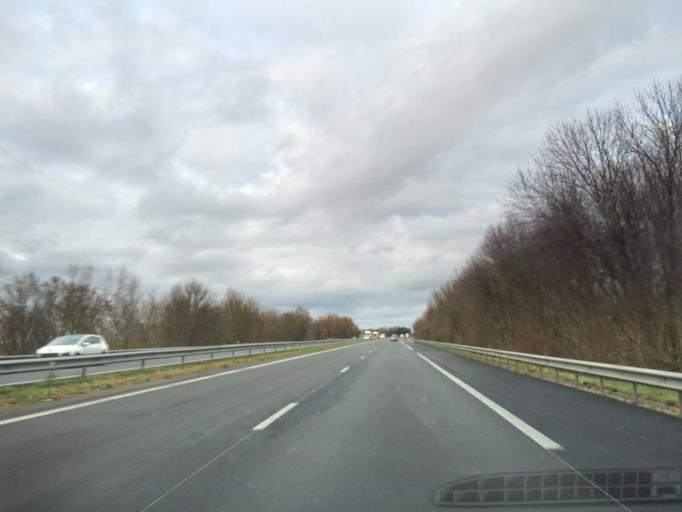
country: FR
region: Poitou-Charentes
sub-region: Departement des Deux-Sevres
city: Aiffres
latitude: 46.2795
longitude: -0.3993
